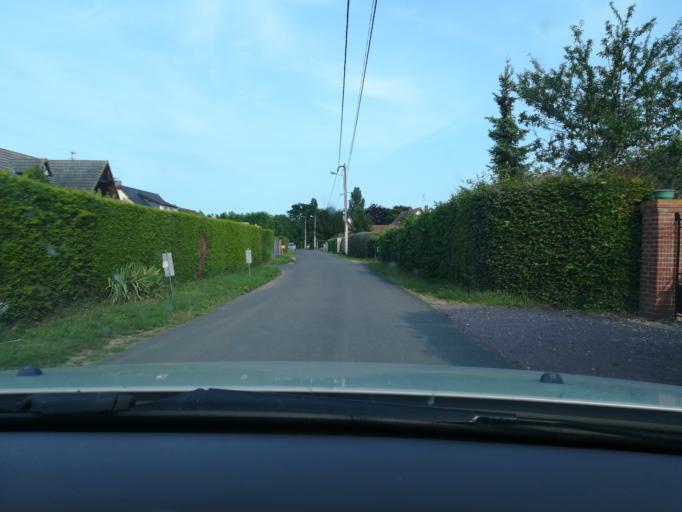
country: FR
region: Haute-Normandie
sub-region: Departement de la Seine-Maritime
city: Sahurs
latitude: 49.3628
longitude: 0.9457
